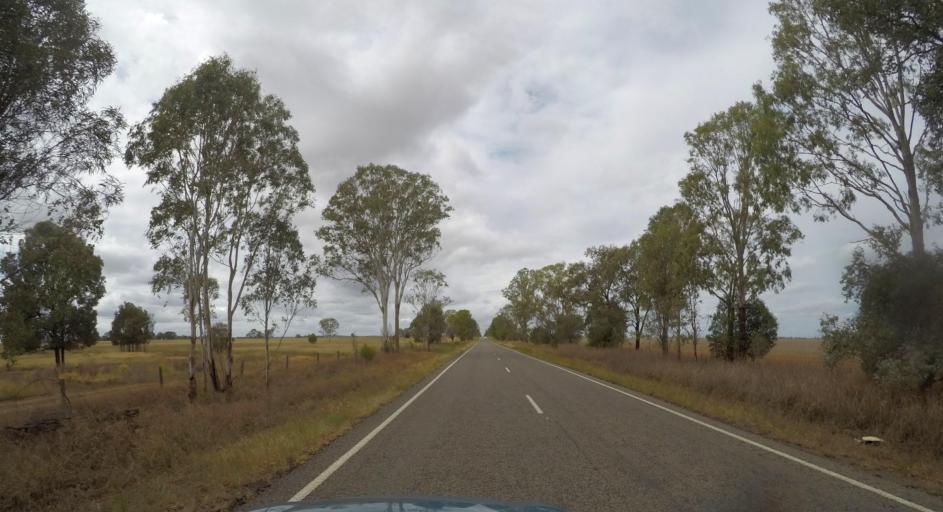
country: AU
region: Queensland
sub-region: South Burnett
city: Kingaroy
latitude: -26.3926
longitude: 151.2224
